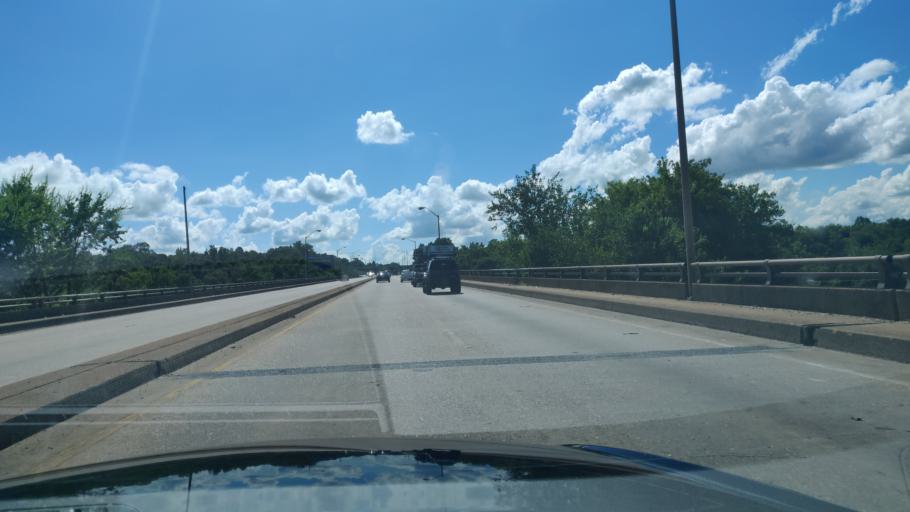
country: US
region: Georgia
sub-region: Muscogee County
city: Columbus
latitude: 32.4532
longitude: -84.9935
